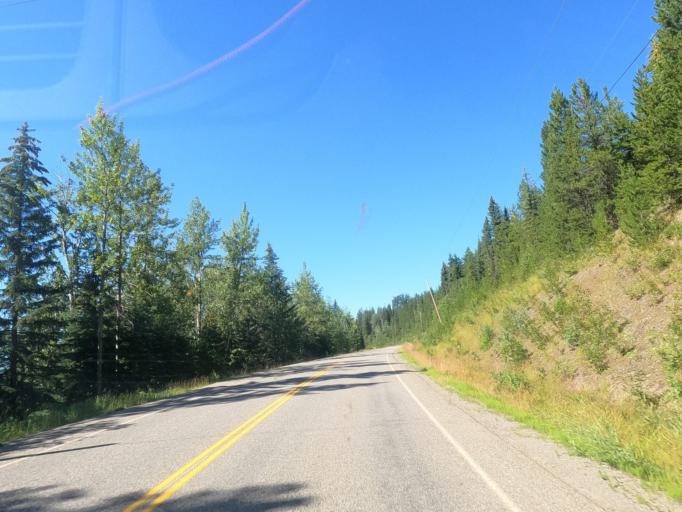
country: CA
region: British Columbia
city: Quesnel
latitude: 53.0343
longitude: -122.0000
